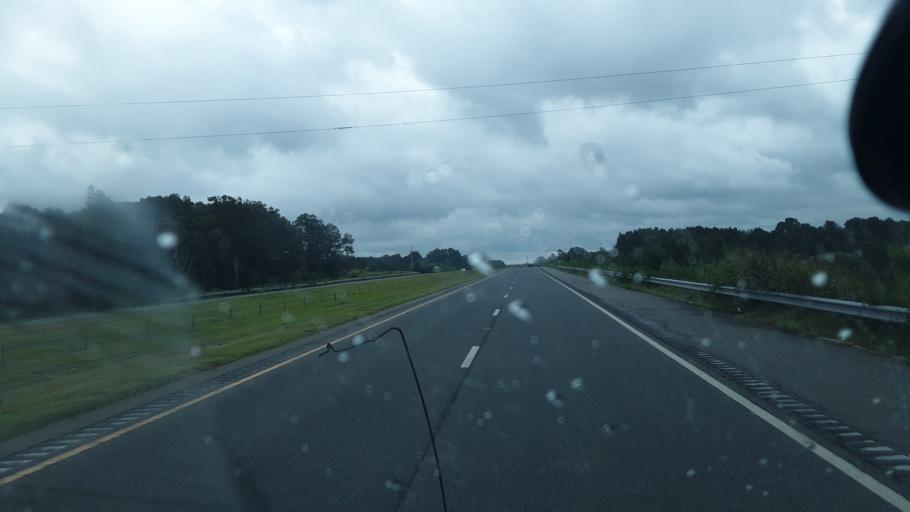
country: US
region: North Carolina
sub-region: Randolph County
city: Randleman
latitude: 35.8074
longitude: -79.8490
